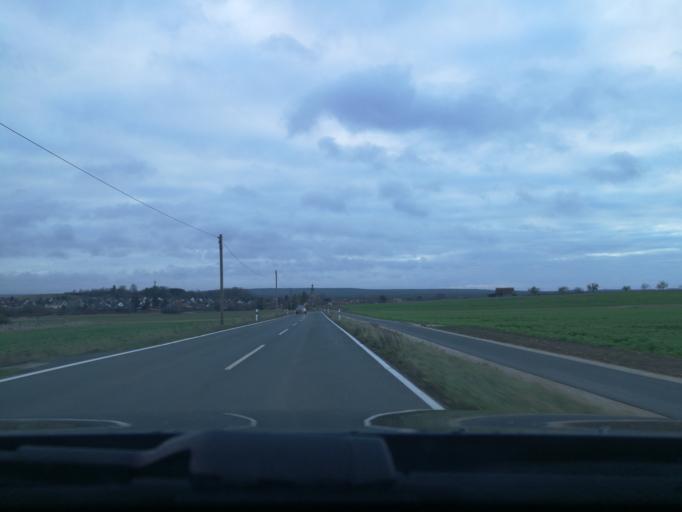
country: DE
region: Bavaria
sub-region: Regierungsbezirk Mittelfranken
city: Uttenreuth
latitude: 49.6068
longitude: 11.0741
